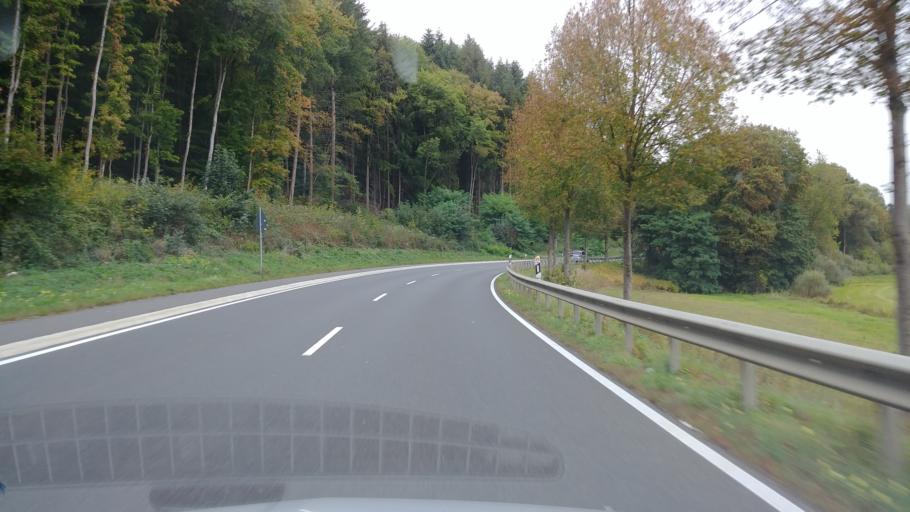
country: DE
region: Rheinland-Pfalz
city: Holzheim
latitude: 50.3573
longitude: 8.0342
